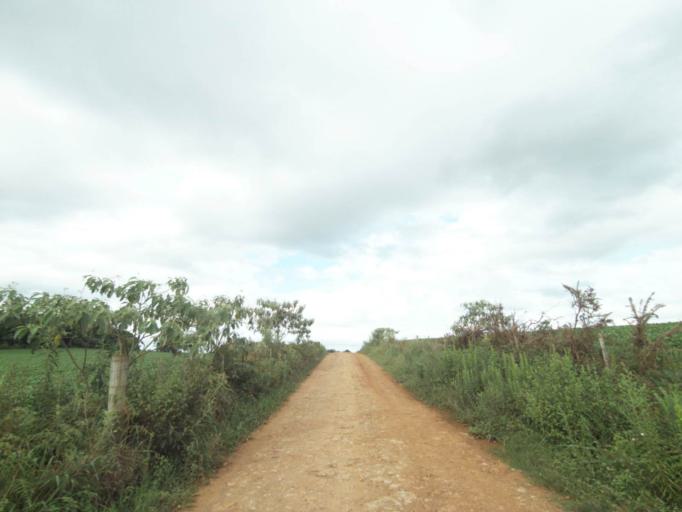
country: BR
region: Rio Grande do Sul
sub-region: Lagoa Vermelha
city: Lagoa Vermelha
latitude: -28.2005
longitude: -51.5140
